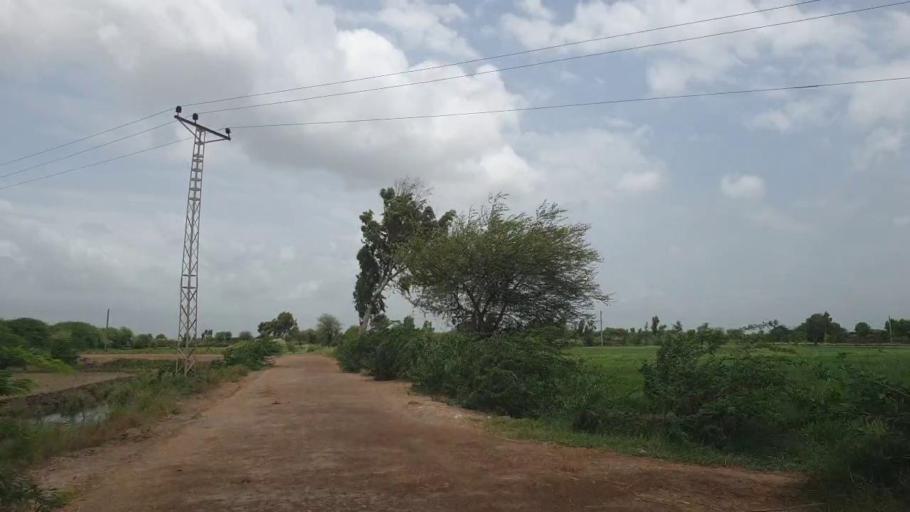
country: PK
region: Sindh
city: Badin
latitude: 24.6661
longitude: 68.8919
